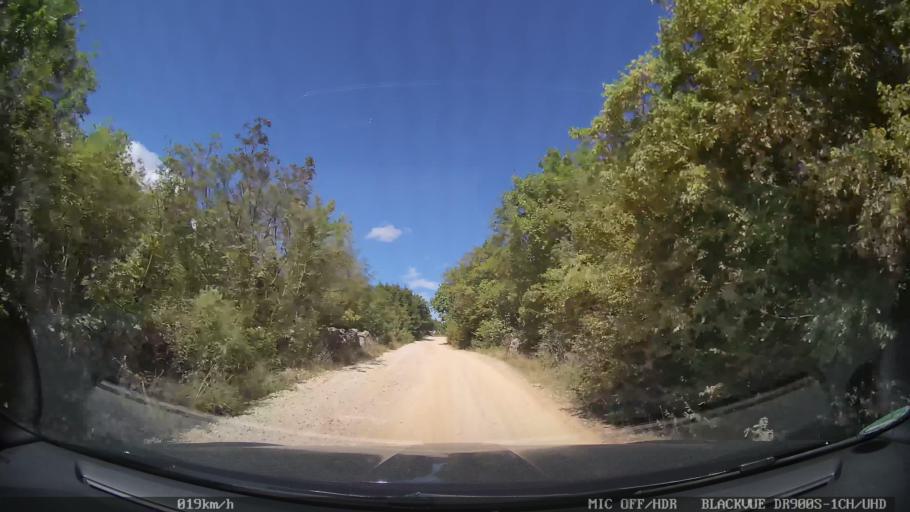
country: HR
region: Primorsko-Goranska
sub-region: Grad Krk
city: Krk
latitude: 45.0369
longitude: 14.5340
